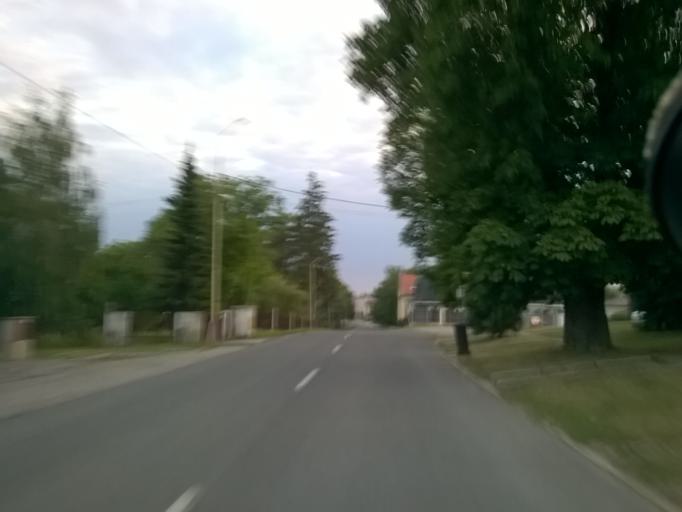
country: SK
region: Trnavsky
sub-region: Okres Senica
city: Senica
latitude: 48.7275
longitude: 17.3476
